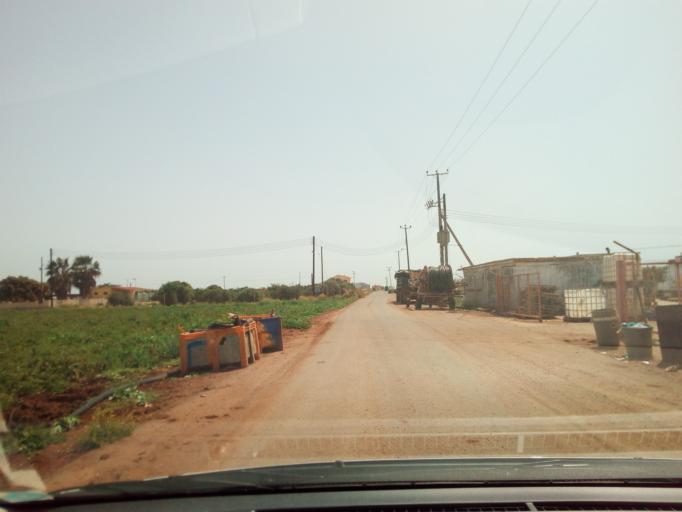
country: CY
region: Ammochostos
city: Avgorou
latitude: 34.9834
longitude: 33.8248
